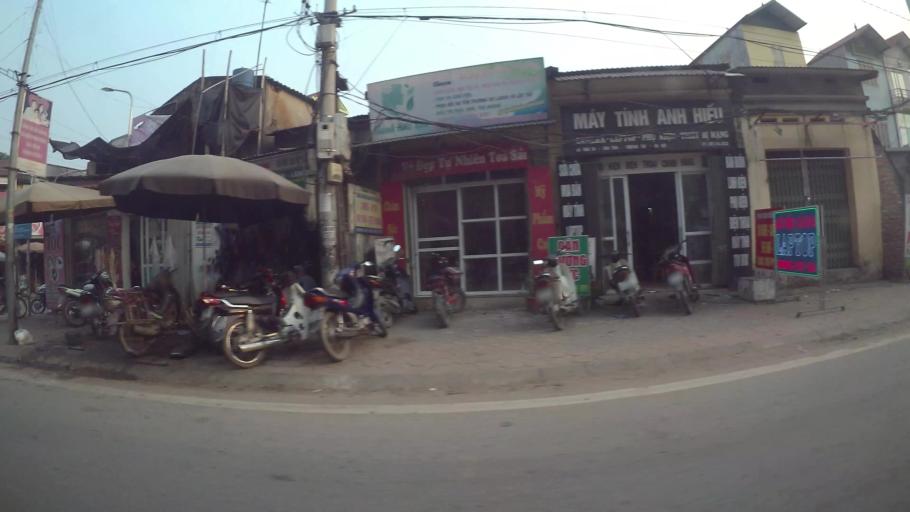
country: VN
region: Ha Noi
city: Thuong Tin
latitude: 20.8676
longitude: 105.8538
